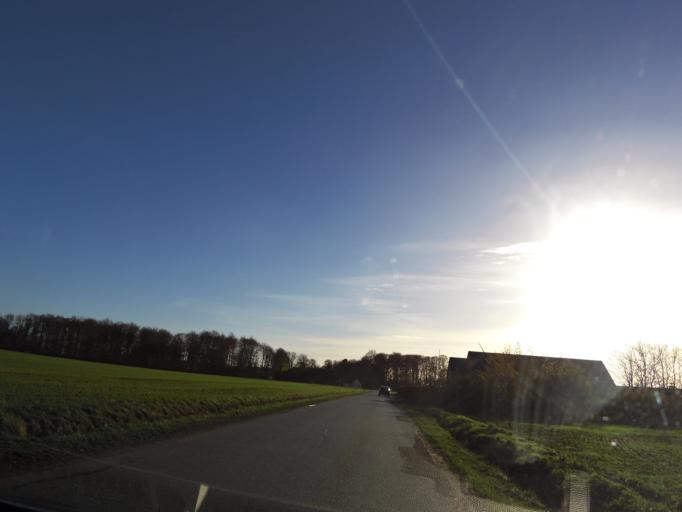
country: DK
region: Central Jutland
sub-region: Odder Kommune
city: Odder
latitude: 55.9191
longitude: 10.2330
